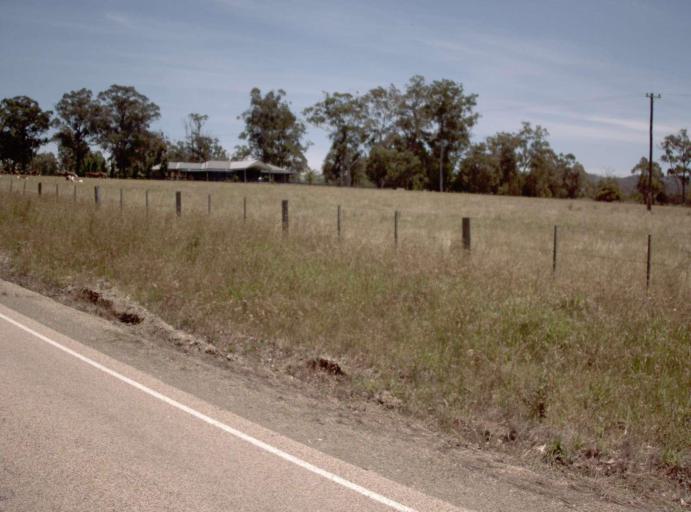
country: AU
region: Victoria
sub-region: East Gippsland
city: Lakes Entrance
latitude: -37.6822
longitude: 147.8457
